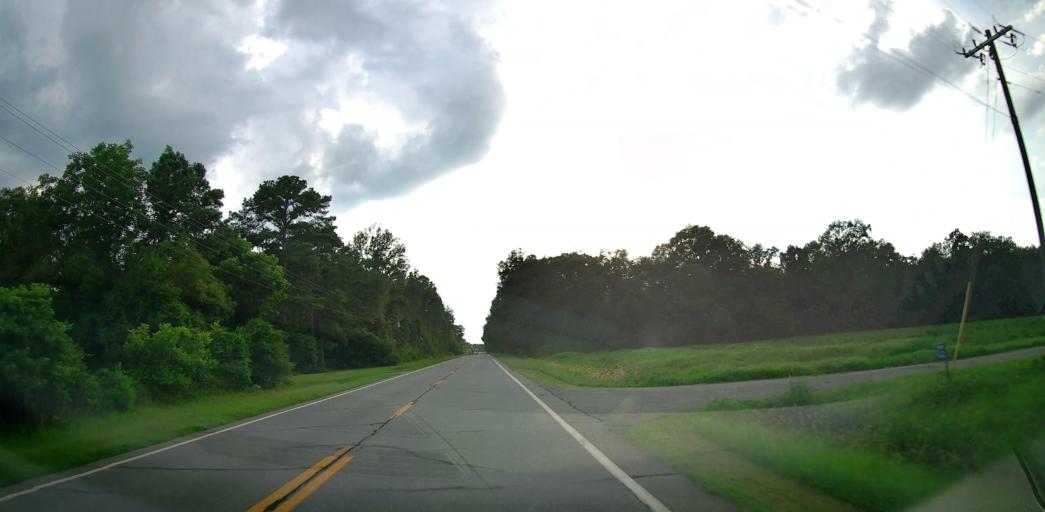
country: US
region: Georgia
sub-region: Pulaski County
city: Hawkinsville
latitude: 32.2955
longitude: -83.5475
